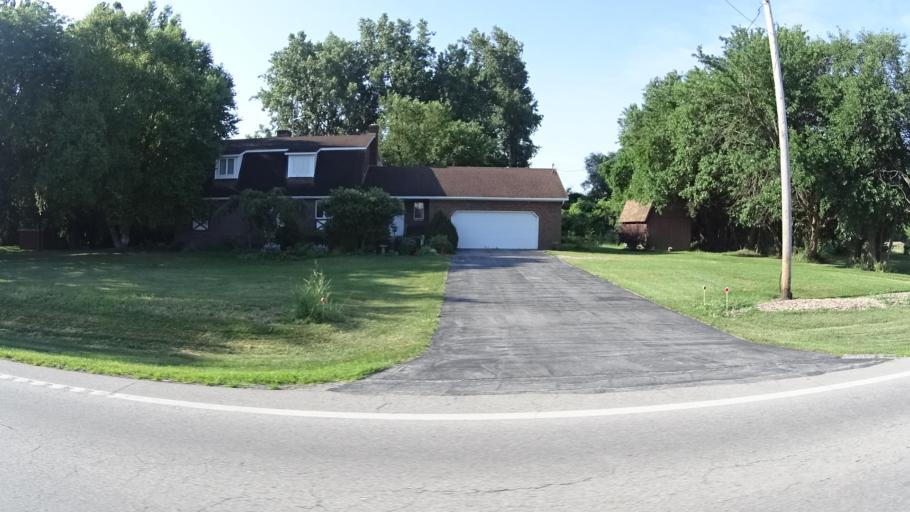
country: US
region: Ohio
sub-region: Erie County
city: Sandusky
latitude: 41.4405
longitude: -82.7852
